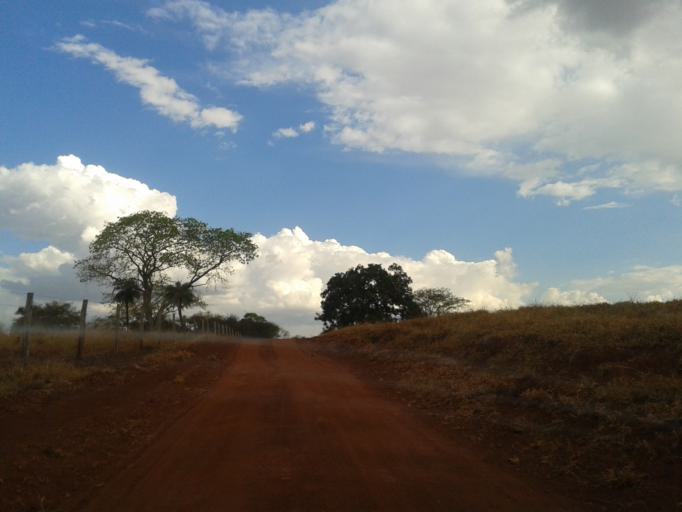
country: BR
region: Minas Gerais
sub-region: Santa Vitoria
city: Santa Vitoria
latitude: -19.1766
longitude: -49.9455
